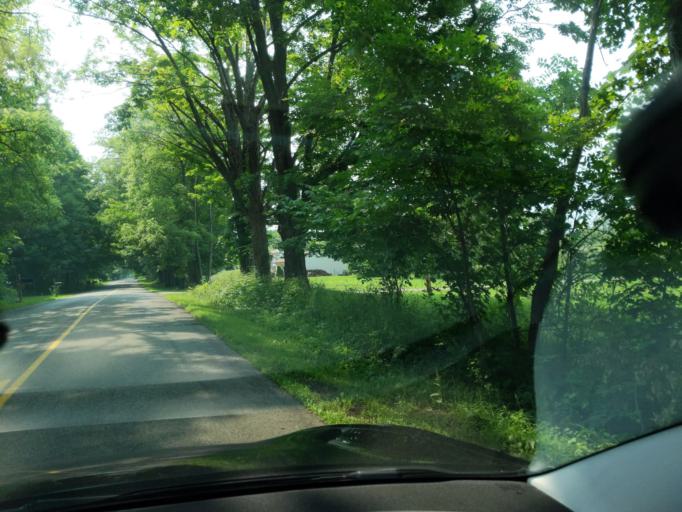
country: US
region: Michigan
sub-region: Ingham County
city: Holt
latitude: 42.6114
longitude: -84.5726
